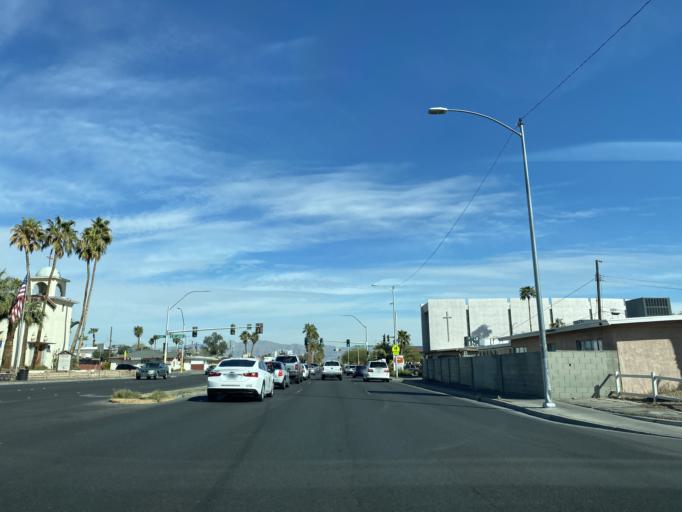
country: US
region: Nevada
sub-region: Clark County
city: Winchester
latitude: 36.1471
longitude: -115.1370
